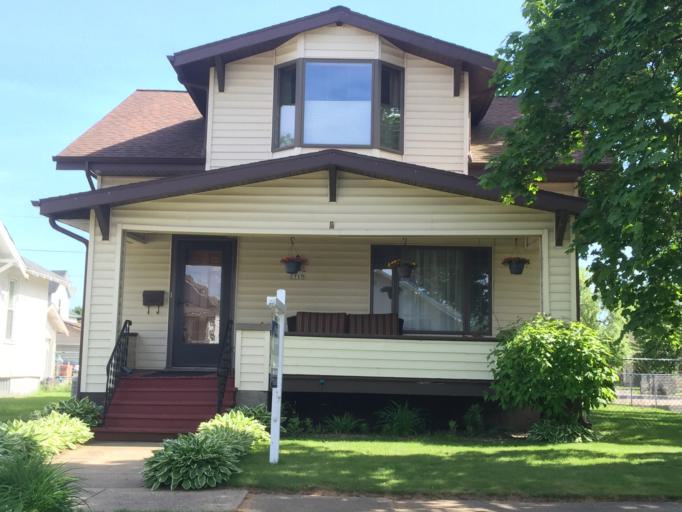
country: US
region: Michigan
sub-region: Menominee County
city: Menominee
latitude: 45.1134
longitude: -87.6247
